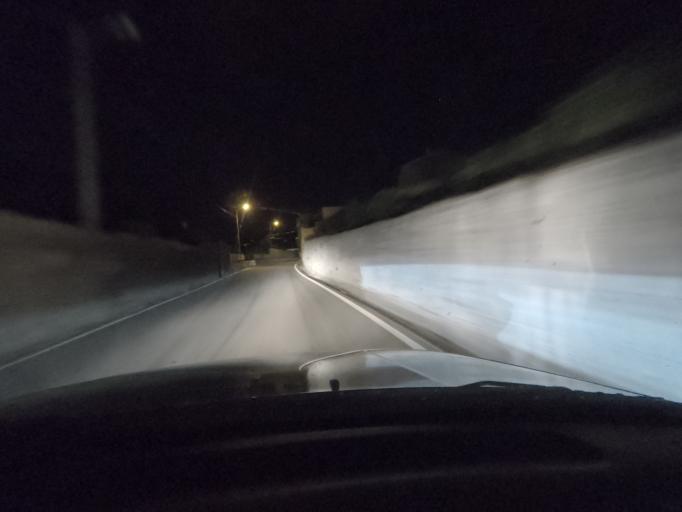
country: PT
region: Vila Real
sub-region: Peso da Regua
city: Godim
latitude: 41.1857
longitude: -7.7932
